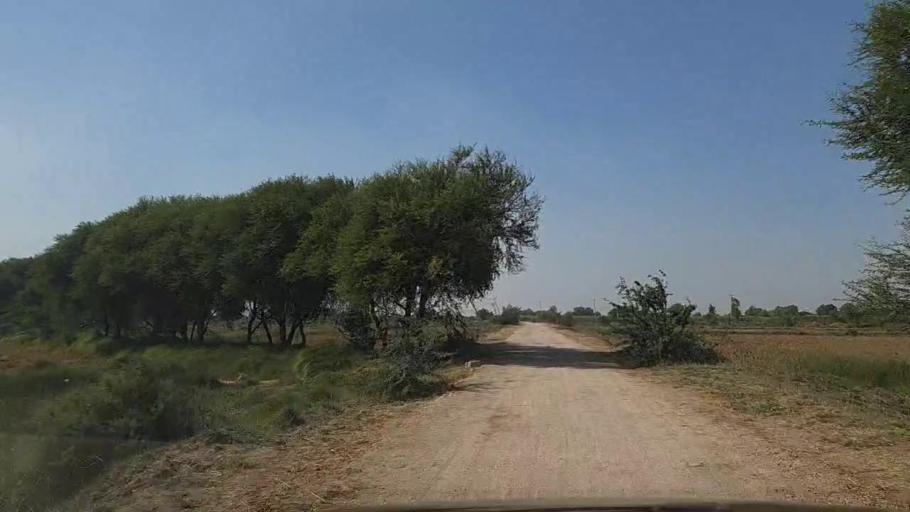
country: PK
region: Sindh
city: Daro Mehar
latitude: 24.8377
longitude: 68.1475
